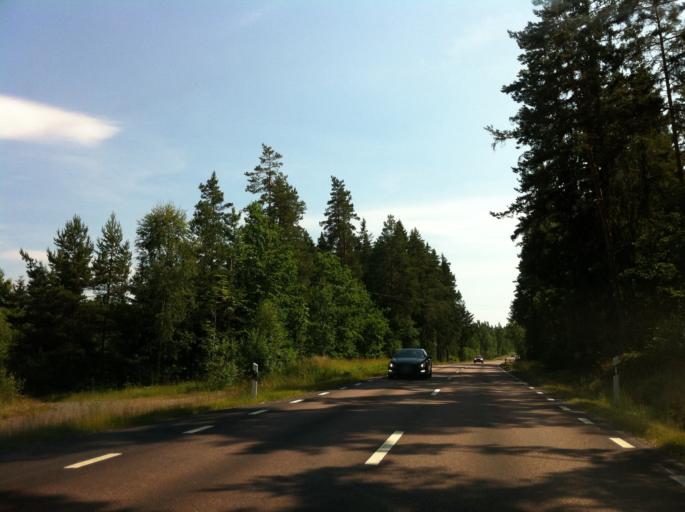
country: SE
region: Kalmar
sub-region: Nybro Kommun
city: Nybro
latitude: 56.8078
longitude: 15.7862
